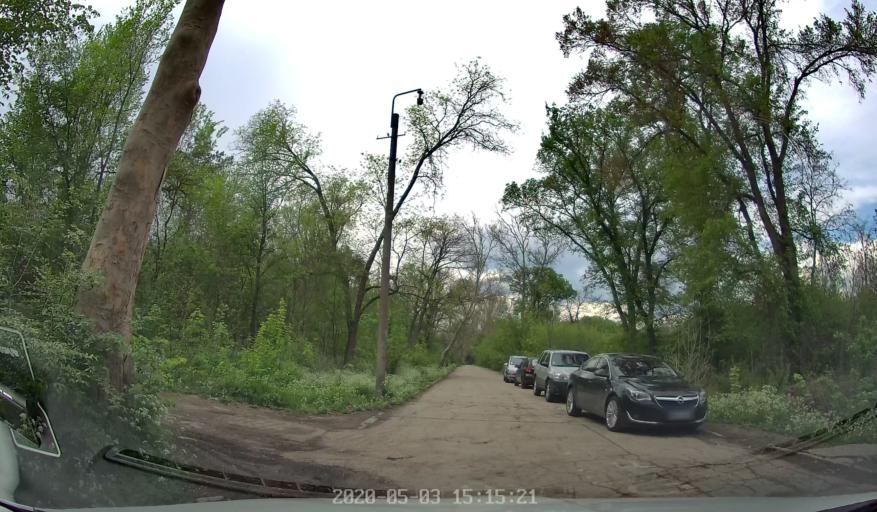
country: MD
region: Chisinau
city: Vatra
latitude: 47.0835
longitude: 28.7185
